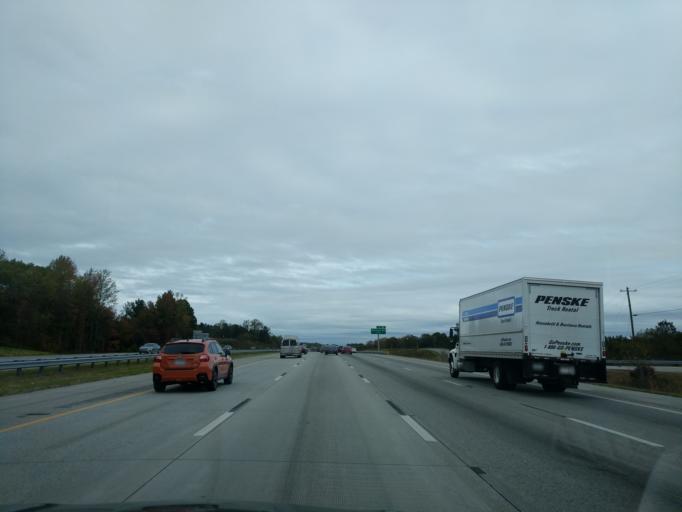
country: US
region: North Carolina
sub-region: Davidson County
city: Tyro
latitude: 35.7394
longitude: -80.3653
